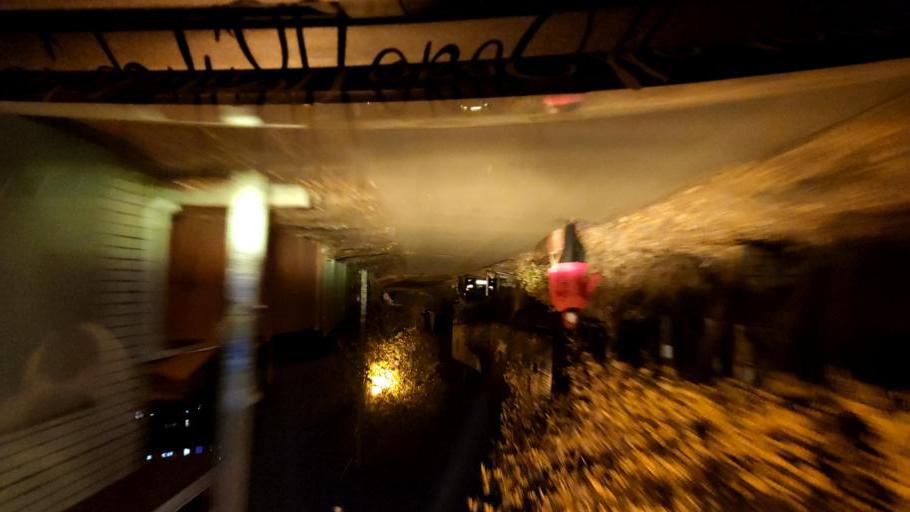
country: RU
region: Voronezj
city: Voronezh
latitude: 51.6910
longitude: 39.2200
